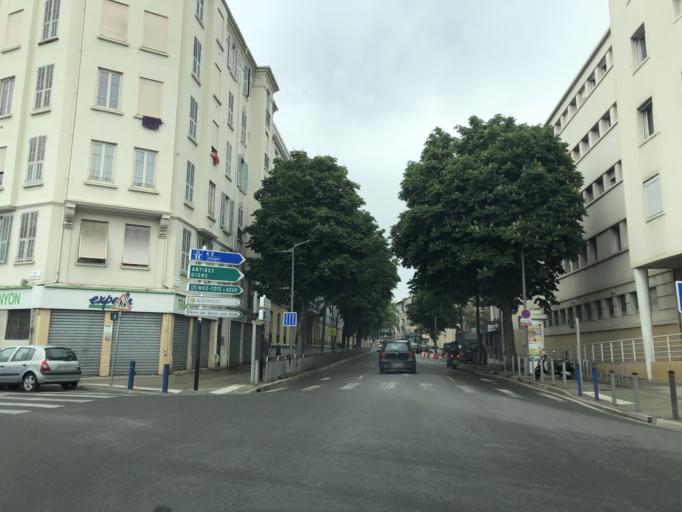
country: FR
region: Provence-Alpes-Cote d'Azur
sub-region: Departement des Alpes-Maritimes
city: Nice
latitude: 43.7073
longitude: 7.2862
